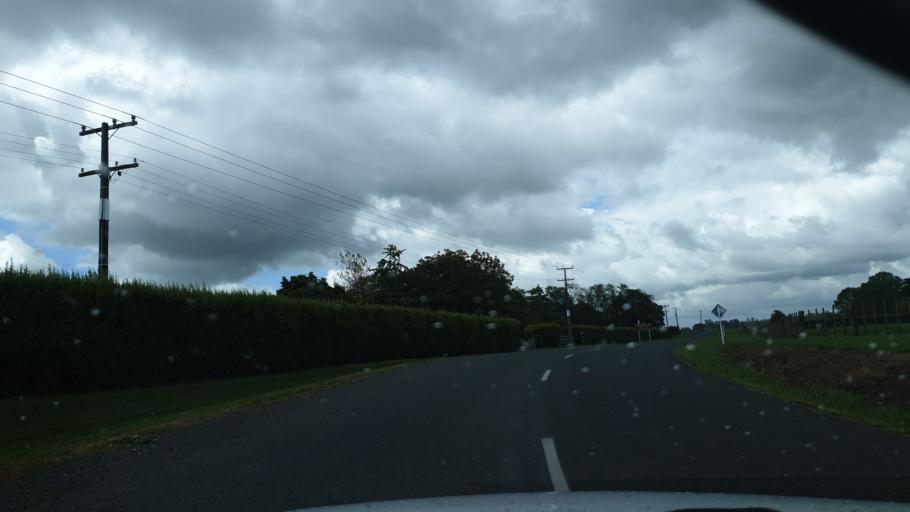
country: NZ
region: Waikato
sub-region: Matamata-Piako District
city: Matamata
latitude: -37.8713
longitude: 175.7242
